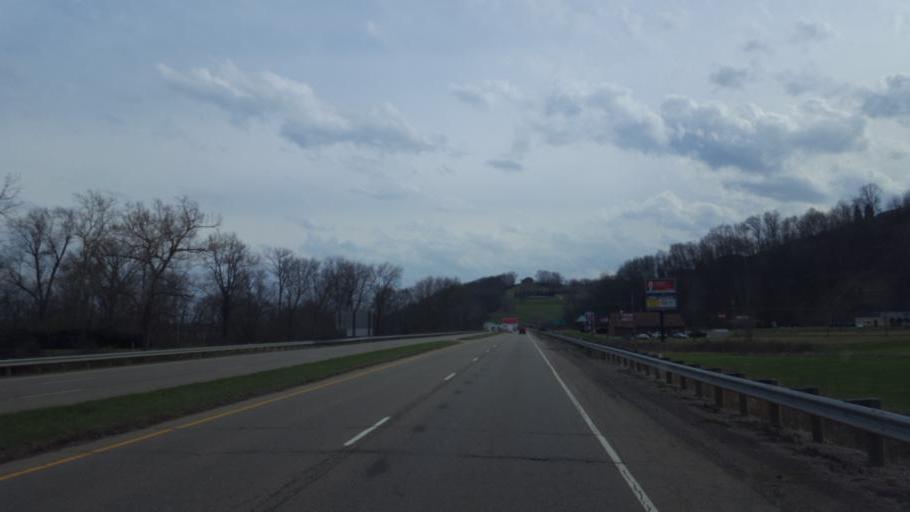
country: US
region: Ohio
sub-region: Coshocton County
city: Coshocton
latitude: 40.2731
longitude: -81.8764
